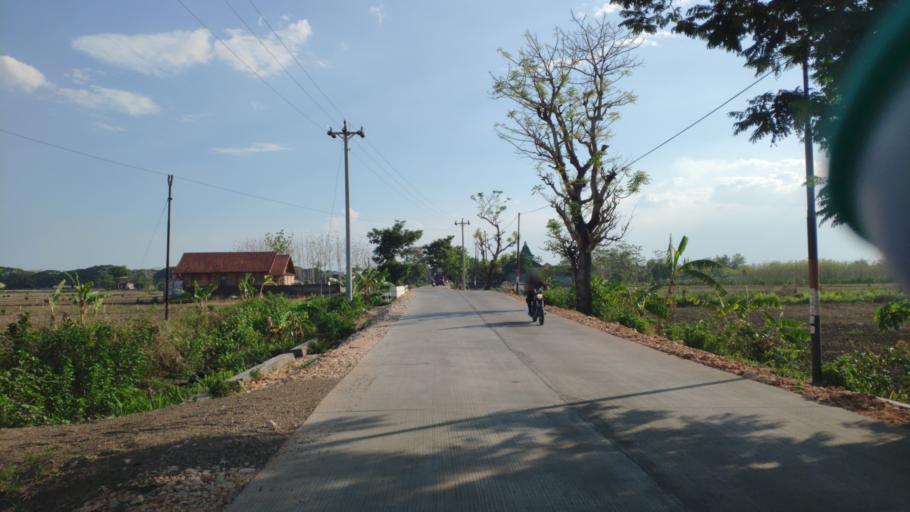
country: ID
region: Central Java
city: Wulung
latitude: -7.1830
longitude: 111.3993
